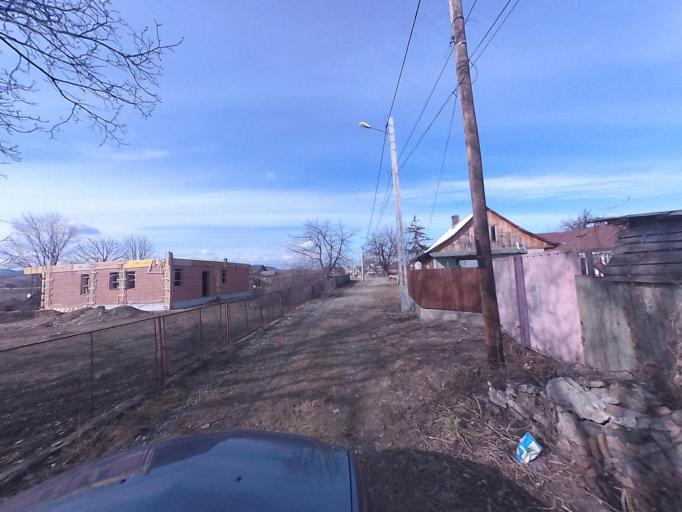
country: RO
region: Neamt
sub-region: Oras Targu Neamt
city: Humulesti
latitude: 47.2124
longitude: 26.3365
